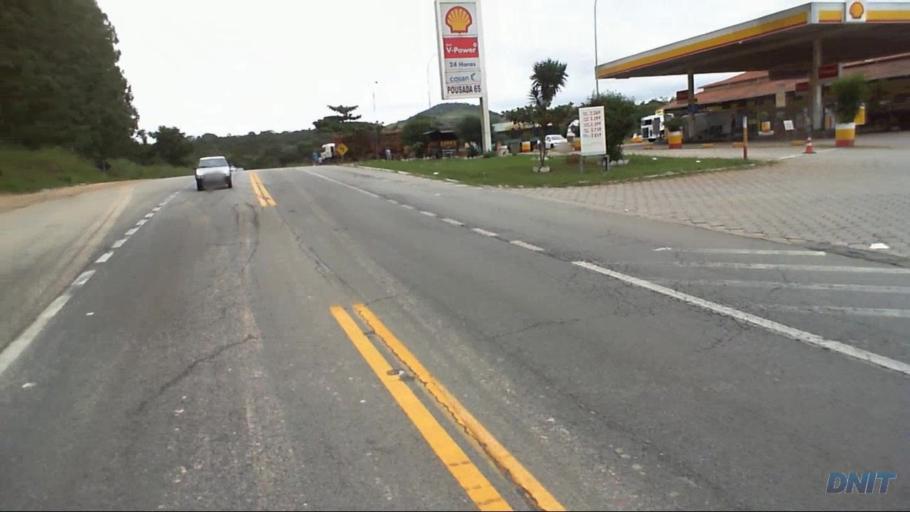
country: BR
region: Minas Gerais
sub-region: Barao De Cocais
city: Barao de Cocais
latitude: -19.7469
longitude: -43.4929
